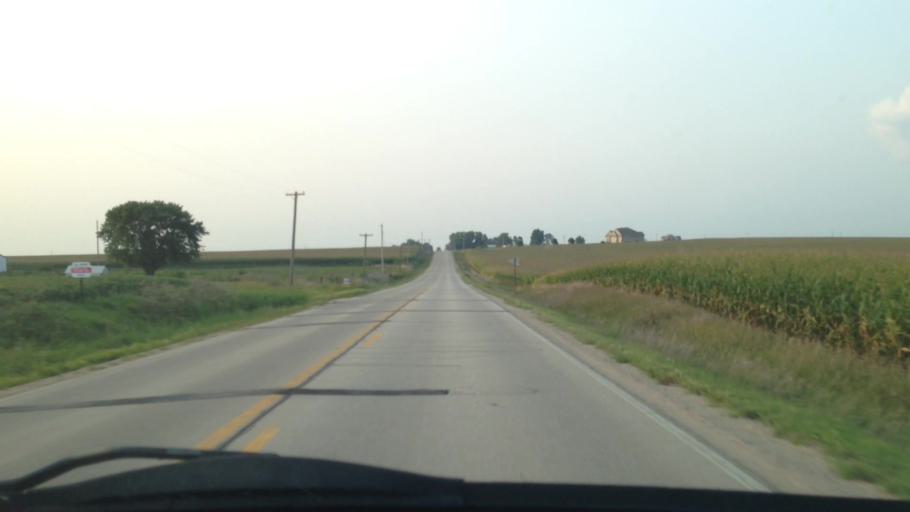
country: US
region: Iowa
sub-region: Benton County
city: Atkins
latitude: 41.9719
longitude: -91.8727
